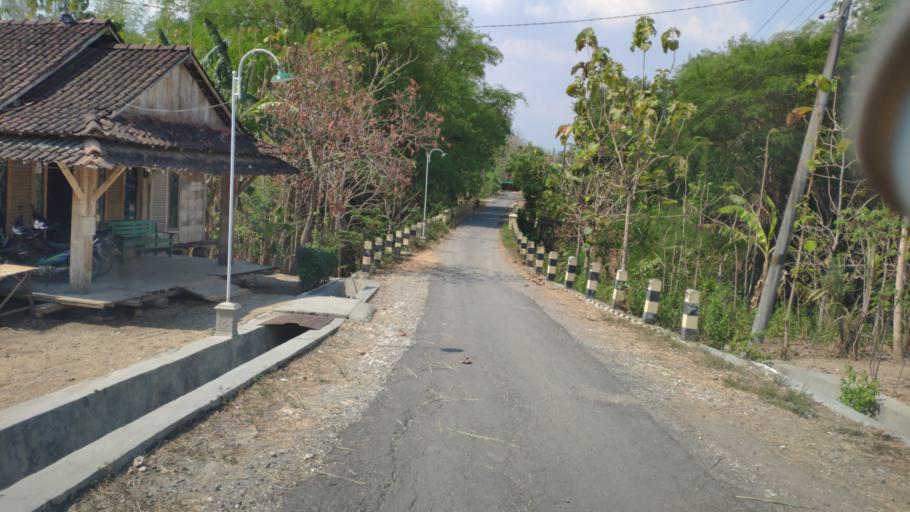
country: ID
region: Central Java
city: Botoh
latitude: -7.0949
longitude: 111.4746
